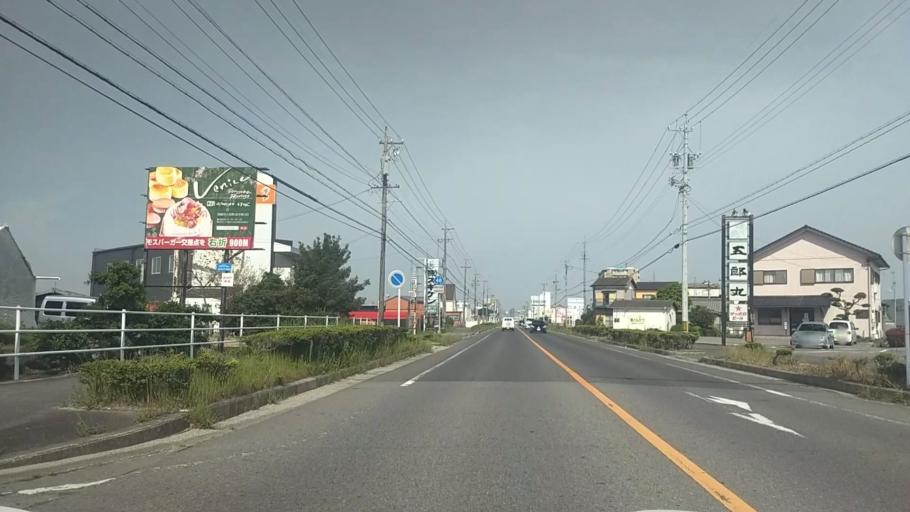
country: JP
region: Aichi
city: Okazaki
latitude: 34.9424
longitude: 137.1288
